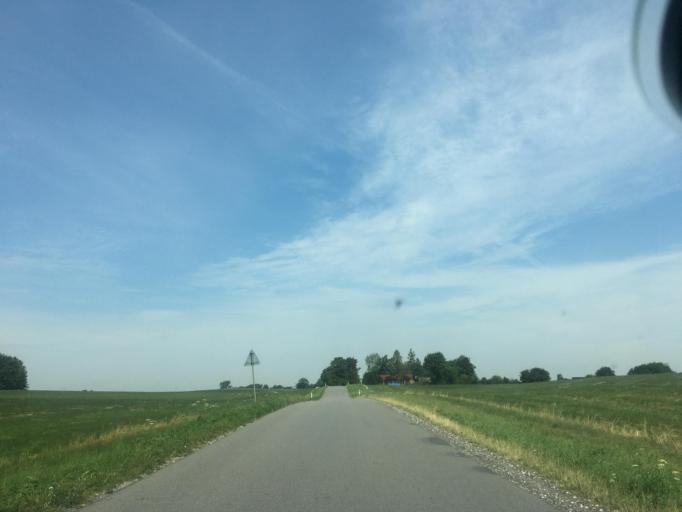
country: DK
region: Zealand
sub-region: Faxe Kommune
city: Ronnede
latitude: 55.2056
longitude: 12.0156
